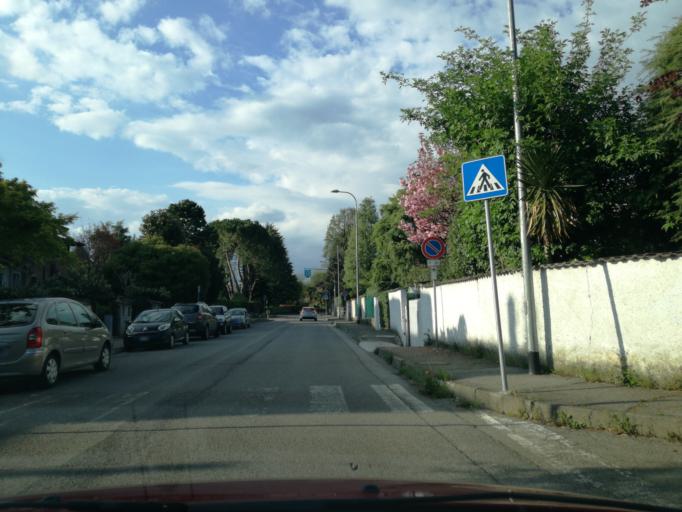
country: IT
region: Lombardy
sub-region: Provincia di Monza e Brianza
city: Carnate
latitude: 45.6419
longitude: 9.3759
